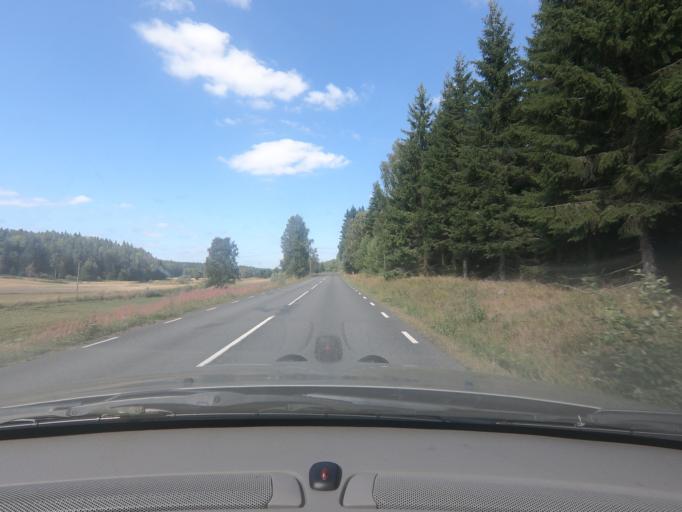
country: SE
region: Joenkoeping
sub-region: Vetlanda Kommun
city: Landsbro
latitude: 57.3376
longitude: 14.8709
